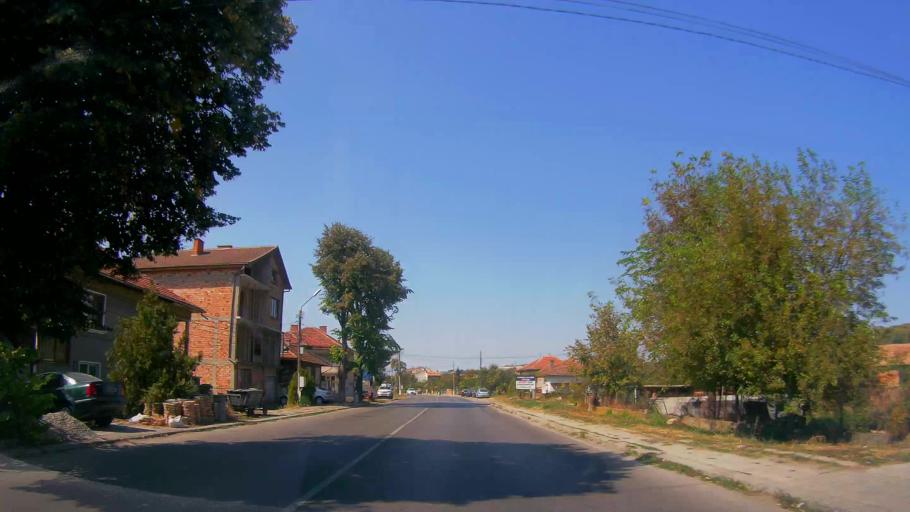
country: BG
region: Razgrad
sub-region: Obshtina Tsar Kaloyan
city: Tsar Kaloyan
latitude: 43.6103
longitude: 26.2340
